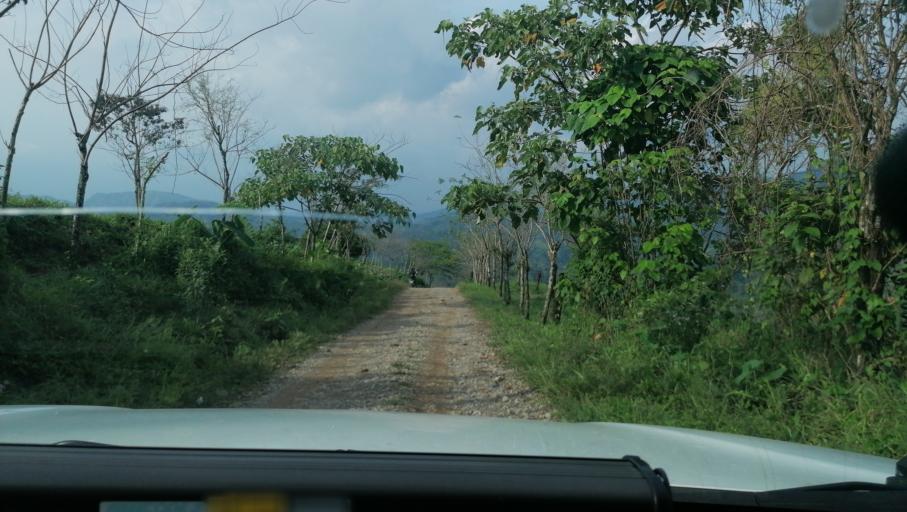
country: MX
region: Chiapas
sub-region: Tapilula
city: San Francisco Jacona
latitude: 17.3215
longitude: -93.0994
